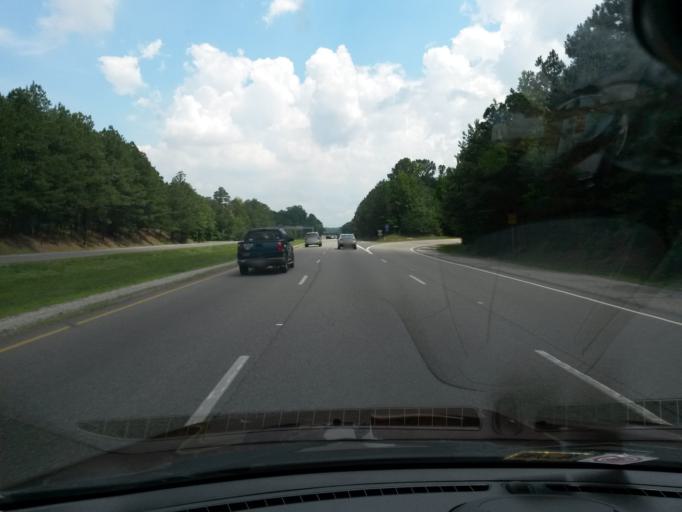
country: US
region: Virginia
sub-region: Chesterfield County
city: Enon
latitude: 37.3414
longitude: -77.3340
